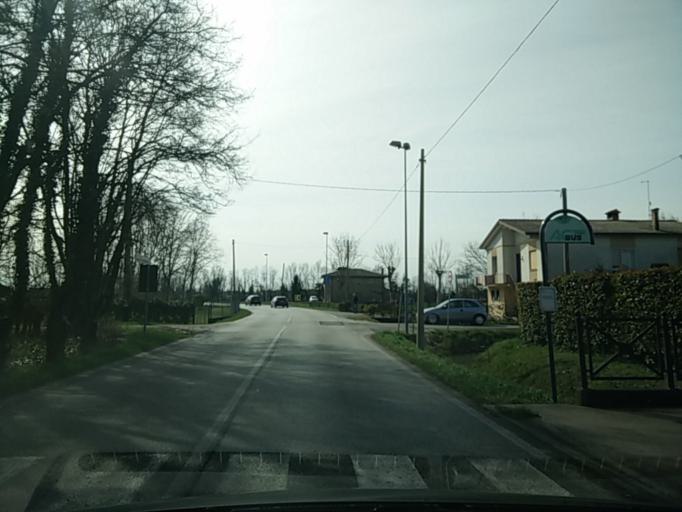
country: IT
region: Veneto
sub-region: Provincia di Treviso
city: Mignagola
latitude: 45.6972
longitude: 12.3217
